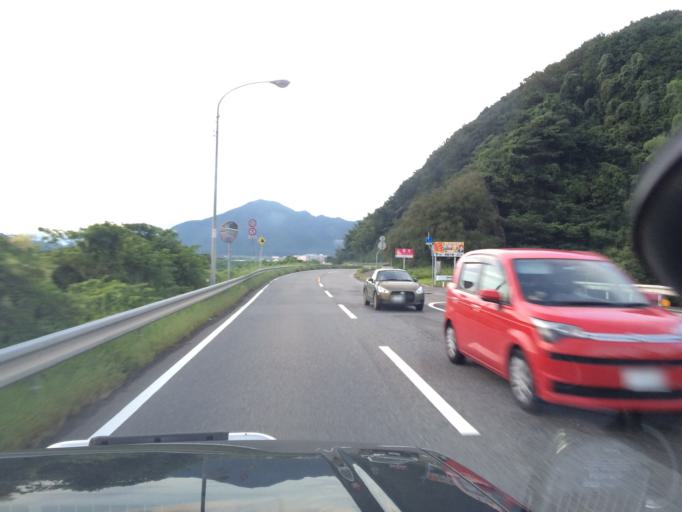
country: JP
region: Kyoto
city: Fukuchiyama
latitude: 35.1492
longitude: 135.0377
